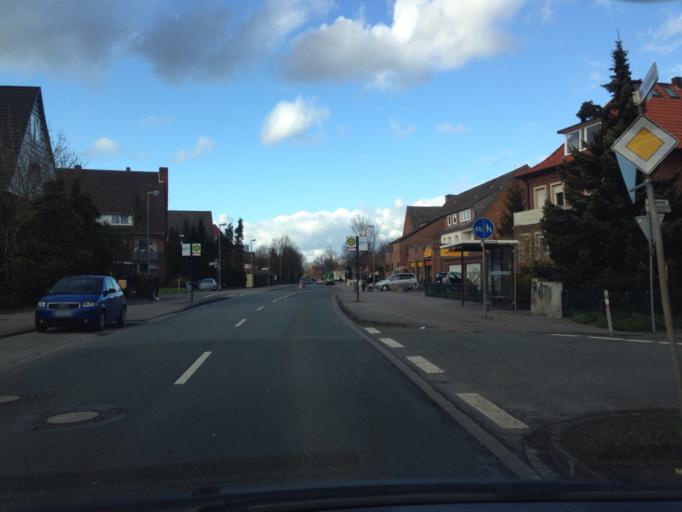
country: DE
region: North Rhine-Westphalia
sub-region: Regierungsbezirk Munster
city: Muenster
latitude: 51.9797
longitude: 7.6442
